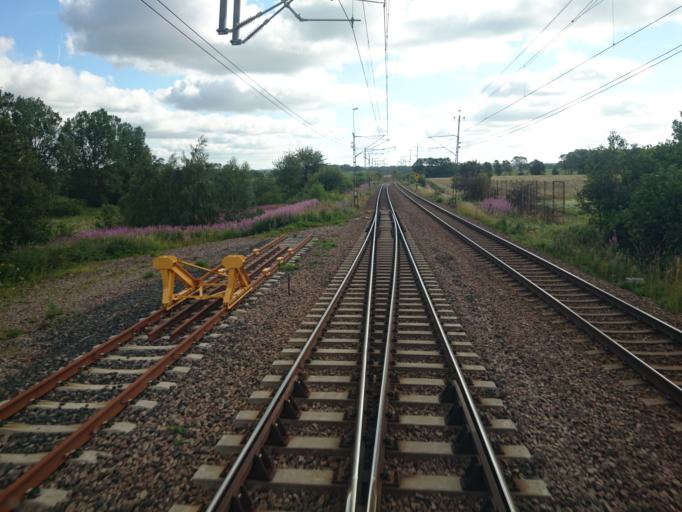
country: SE
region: Skane
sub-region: Eslovs Kommun
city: Stehag
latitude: 55.9034
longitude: 13.4070
